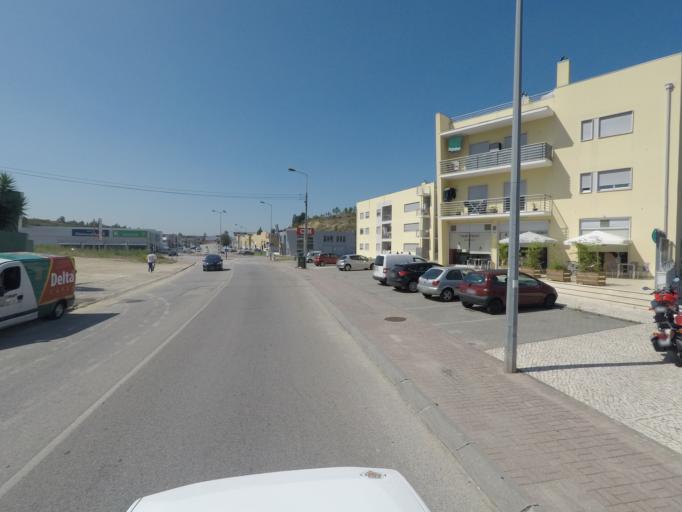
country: PT
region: Coimbra
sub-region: Coimbra
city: Coimbra
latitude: 40.2478
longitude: -8.4282
